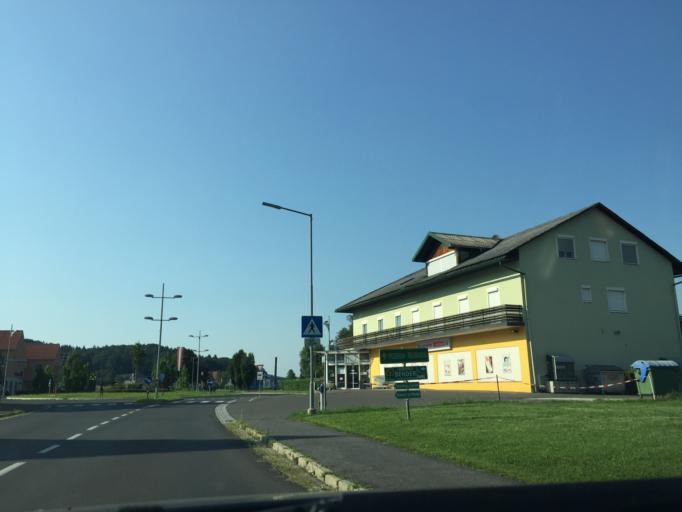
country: AT
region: Styria
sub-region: Politischer Bezirk Suedoststeiermark
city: Deutsch Goritz
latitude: 46.7515
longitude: 15.8302
